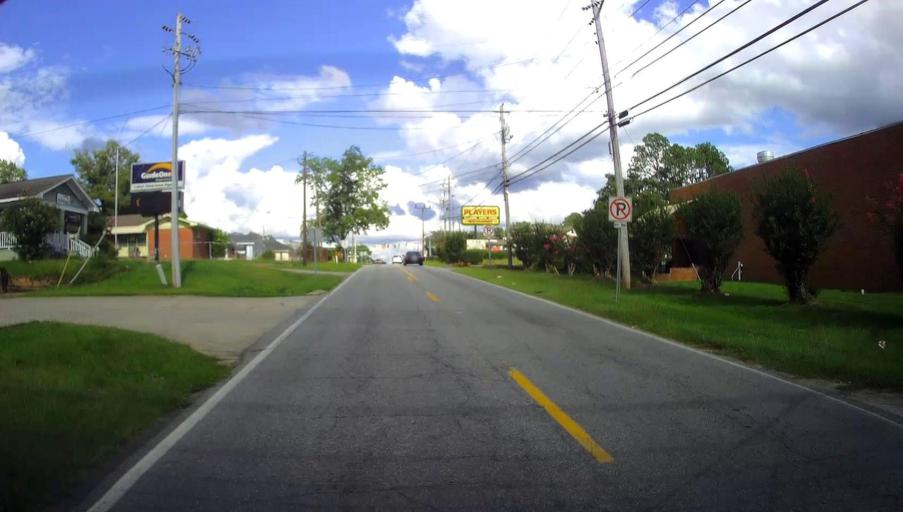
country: US
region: Alabama
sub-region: Russell County
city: Phenix City
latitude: 32.5207
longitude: -84.9665
